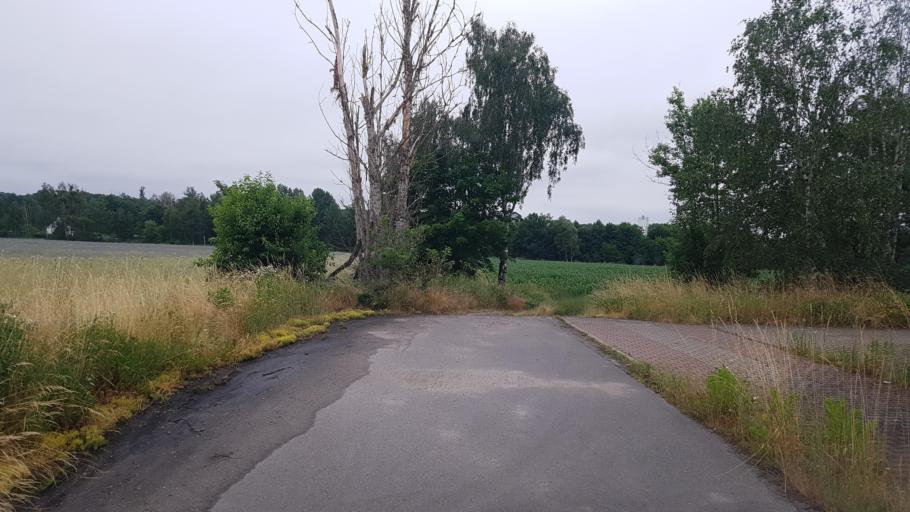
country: DE
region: Brandenburg
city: Senftenberg
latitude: 51.4963
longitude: 13.9603
